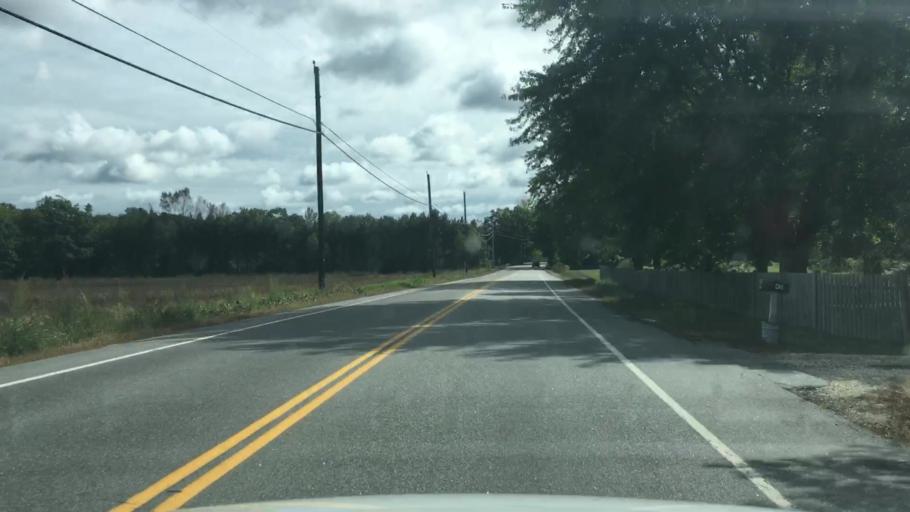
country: US
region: Maine
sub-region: Androscoggin County
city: Lisbon
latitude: 44.0162
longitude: -70.1701
